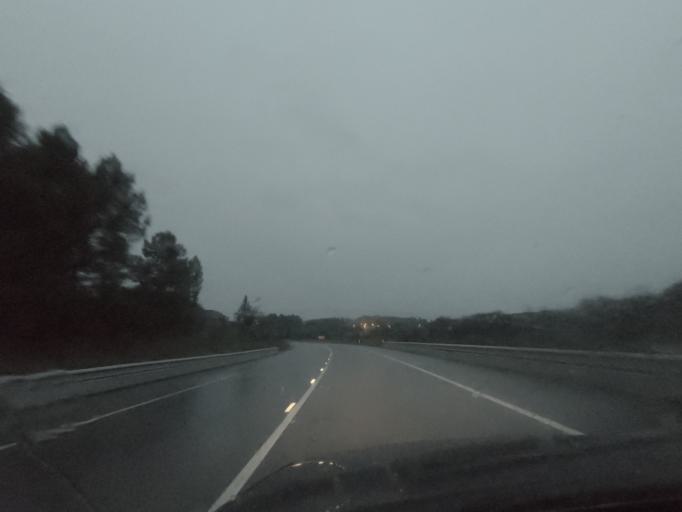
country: PT
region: Vila Real
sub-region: Sabrosa
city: Vilela
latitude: 41.2630
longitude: -7.6584
